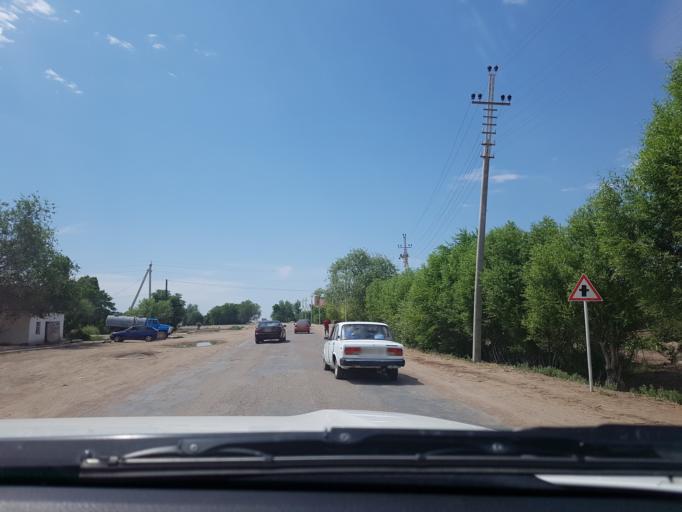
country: TM
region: Dasoguz
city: Koeneuergench
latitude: 42.3148
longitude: 59.1389
